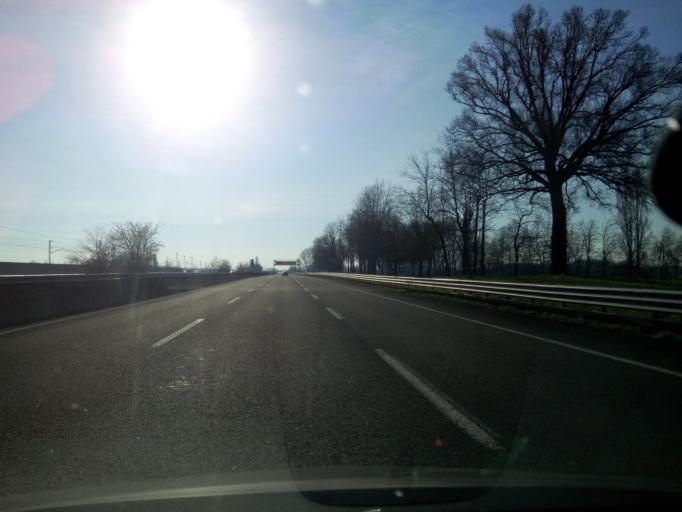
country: IT
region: Emilia-Romagna
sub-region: Provincia di Modena
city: Campogalliano
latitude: 44.6774
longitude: 10.8161
